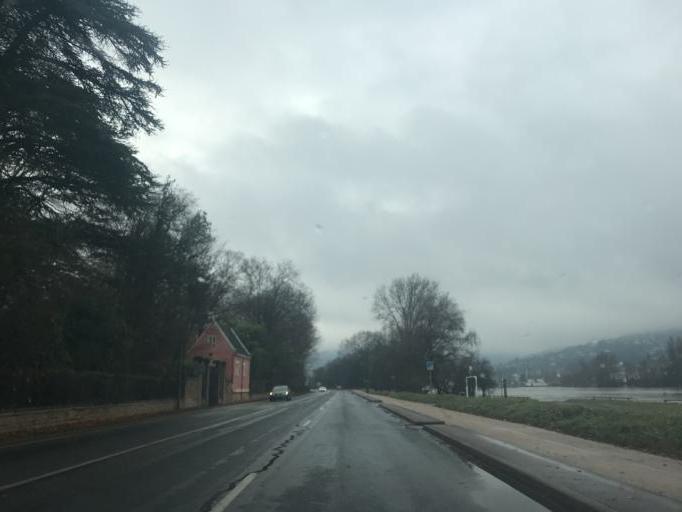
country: FR
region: Rhone-Alpes
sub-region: Departement du Rhone
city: Fleurieu-sur-Saone
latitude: 45.8550
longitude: 4.8395
